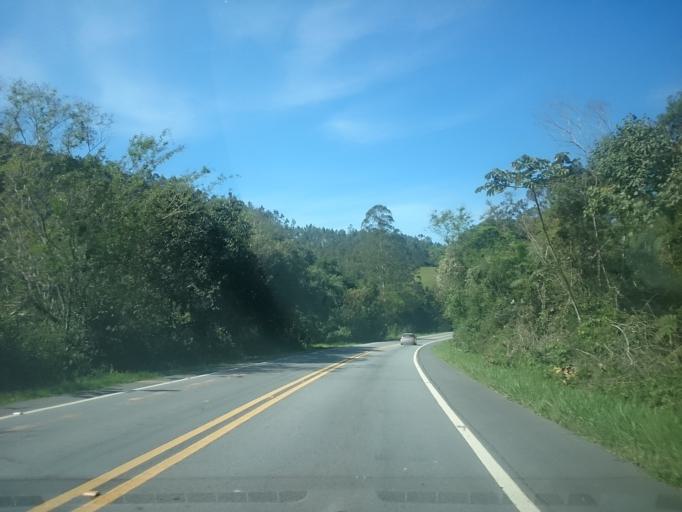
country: BR
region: Santa Catarina
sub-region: Santo Amaro Da Imperatriz
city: Santo Amaro da Imperatriz
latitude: -27.7195
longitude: -48.9001
